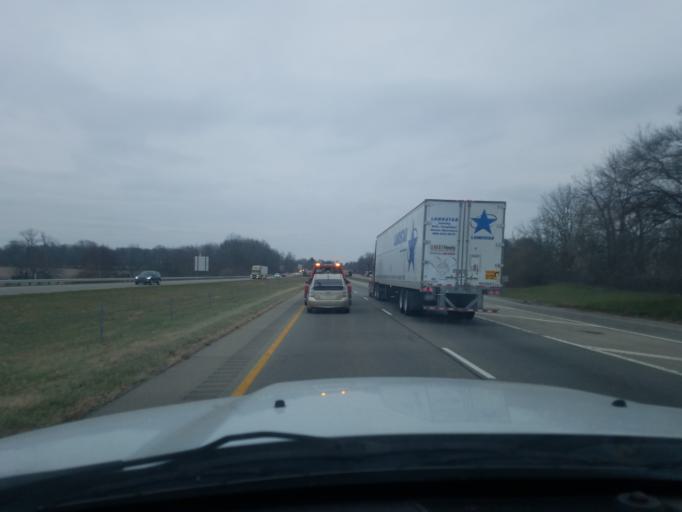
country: US
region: Indiana
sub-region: Bartholomew County
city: Lowell
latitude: 39.2804
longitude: -85.9582
